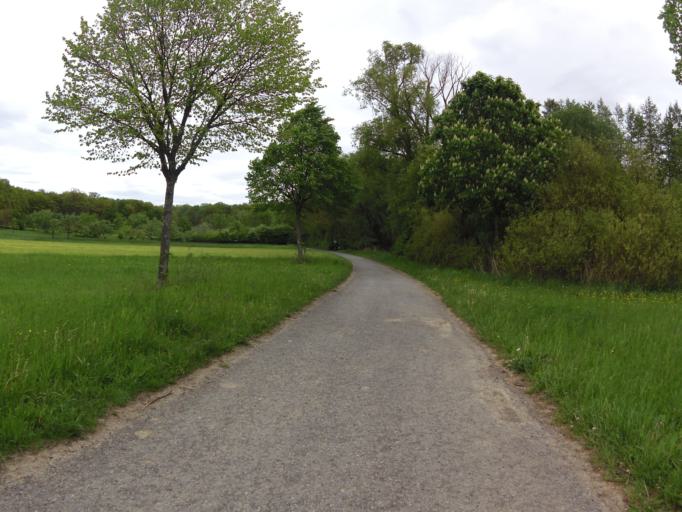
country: DE
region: Bavaria
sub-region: Regierungsbezirk Unterfranken
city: Unterpleichfeld
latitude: 49.8475
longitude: 10.0645
